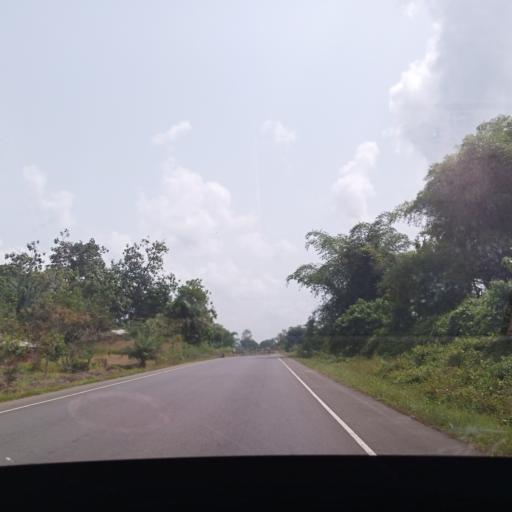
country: LR
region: Margibi
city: Kakata
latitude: 6.2515
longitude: -10.2997
